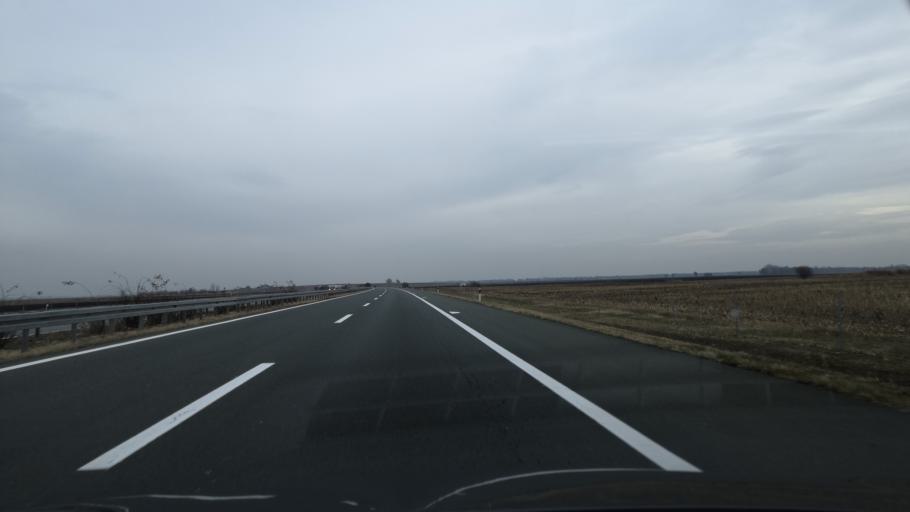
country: RS
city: Zmajevo
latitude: 45.4941
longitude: 19.7289
